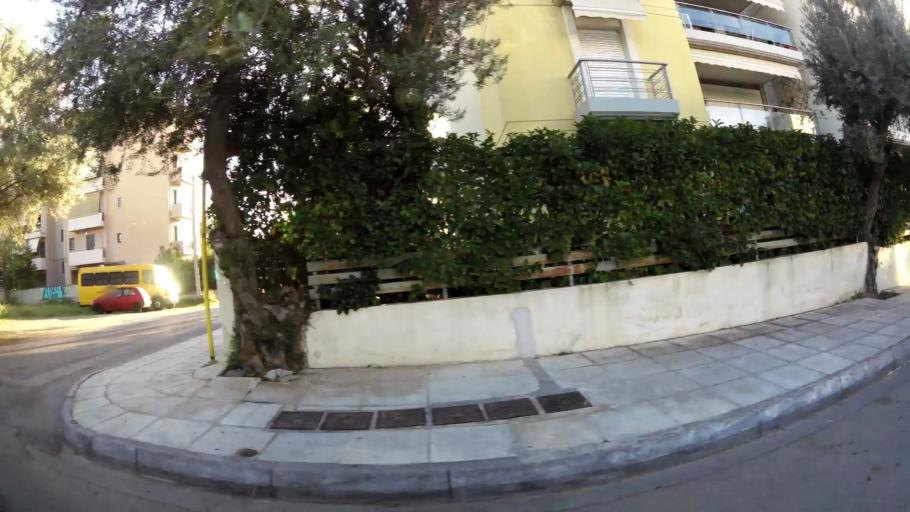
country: GR
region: Attica
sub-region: Nomarchia Athinas
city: Marousi
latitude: 38.0466
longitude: 23.7967
